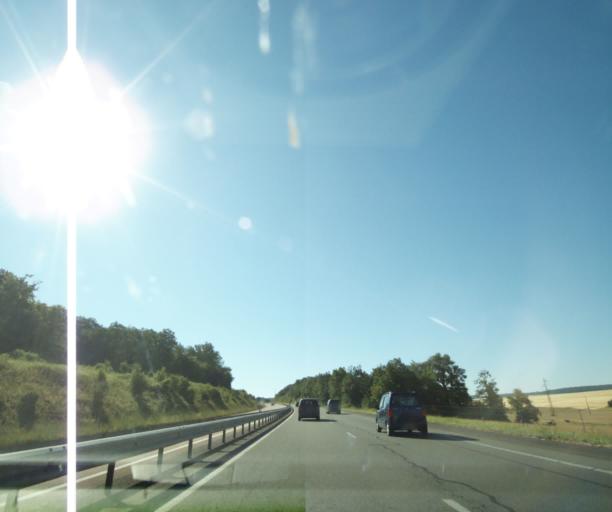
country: FR
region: Champagne-Ardenne
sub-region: Departement de l'Aube
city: Ville-sous-la-Ferte
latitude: 48.0931
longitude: 4.8245
